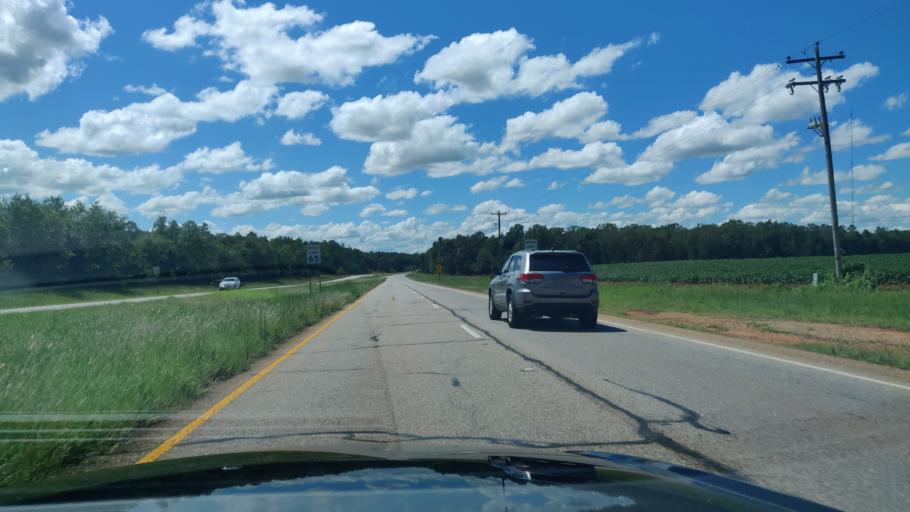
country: US
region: Georgia
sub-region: Webster County
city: Preston
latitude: 31.9214
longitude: -84.5473
